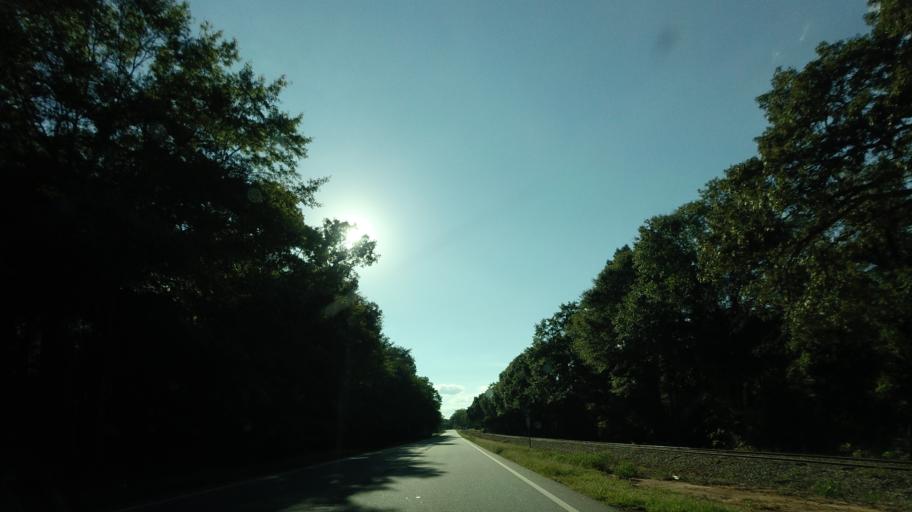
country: US
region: Georgia
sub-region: Lamar County
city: Barnesville
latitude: 32.9647
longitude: -84.2340
